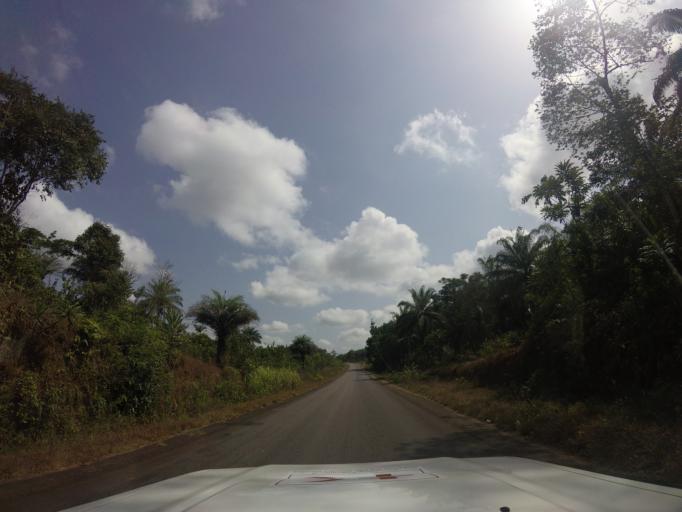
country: LR
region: Grand Cape Mount
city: Robertsport
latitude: 6.7701
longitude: -11.1478
